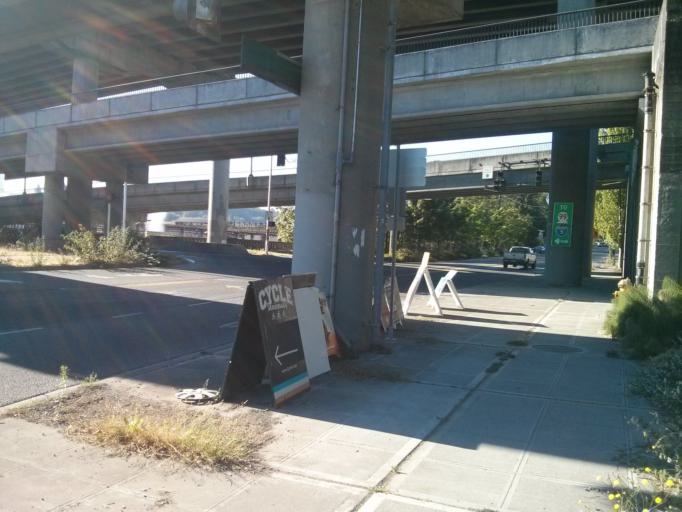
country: US
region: Washington
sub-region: King County
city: Seattle
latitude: 47.5718
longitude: -122.3709
